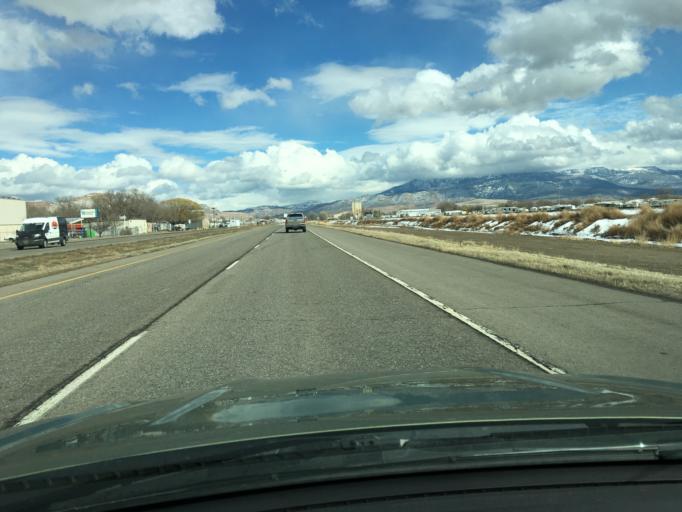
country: US
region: Colorado
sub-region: Mesa County
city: Fruitvale
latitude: 39.0745
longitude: -108.5077
